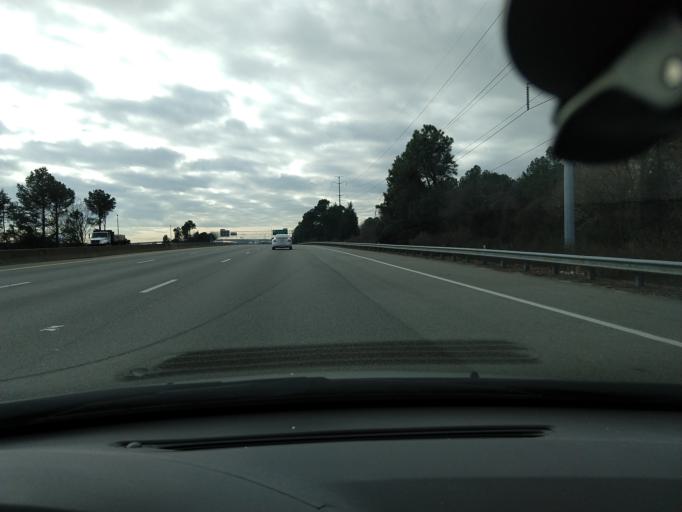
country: US
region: Virginia
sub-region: Chesterfield County
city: Bensley
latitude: 37.4594
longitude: -77.4255
